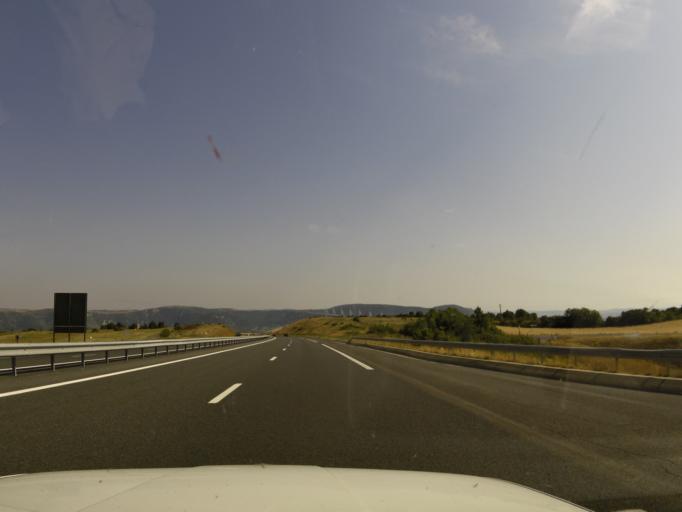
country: FR
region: Midi-Pyrenees
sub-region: Departement de l'Aveyron
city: Creissels
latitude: 44.1188
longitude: 3.0292
